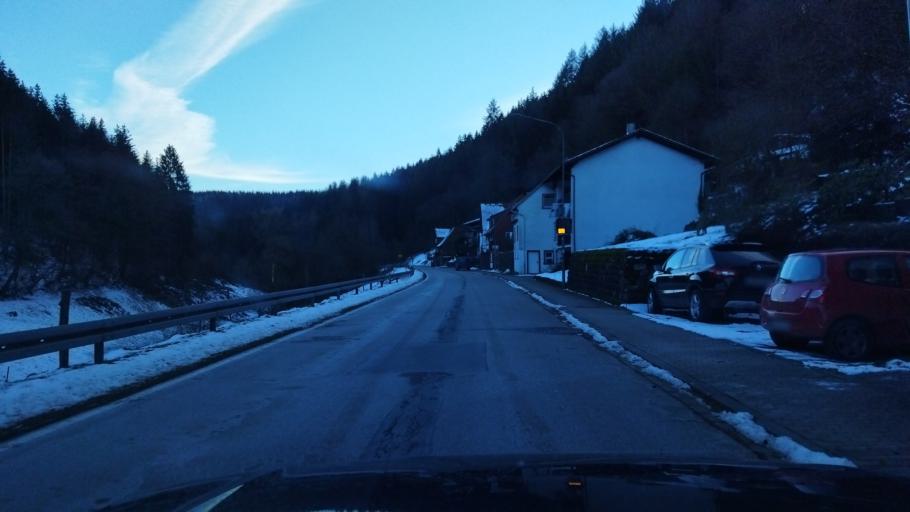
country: DE
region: Baden-Wuerttemberg
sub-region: Karlsruhe Region
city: Eberbach
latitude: 49.5064
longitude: 9.0100
